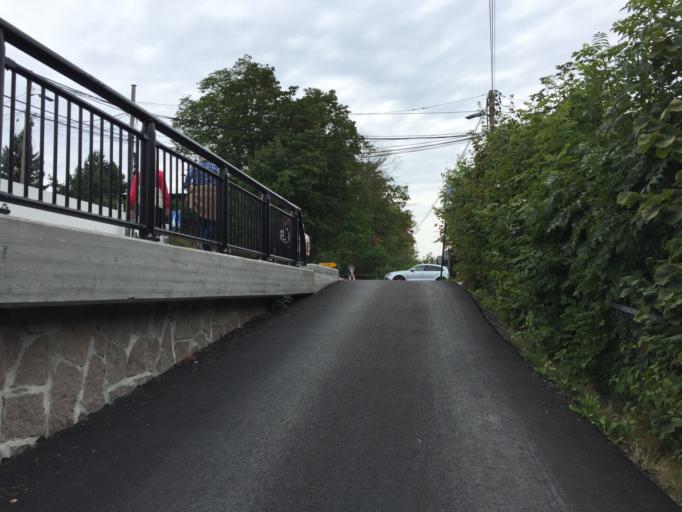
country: NO
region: Oslo
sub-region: Oslo
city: Sjolyststranda
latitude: 59.9017
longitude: 10.6874
